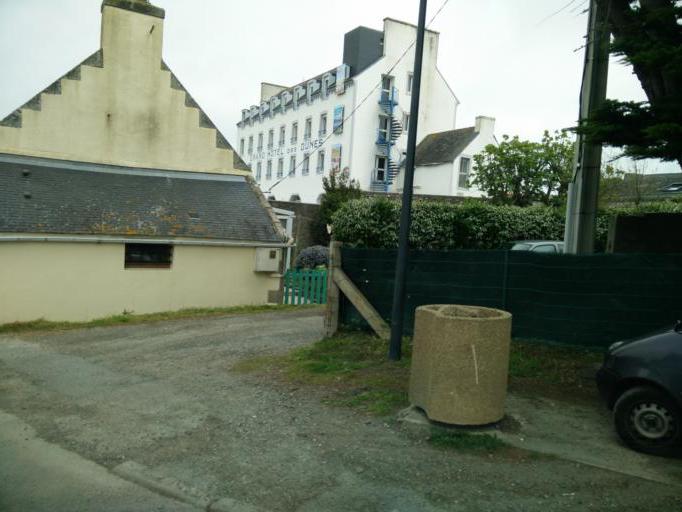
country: FR
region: Brittany
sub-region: Departement du Finistere
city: Plobannalec-Lesconil
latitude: 47.7948
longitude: -4.2202
